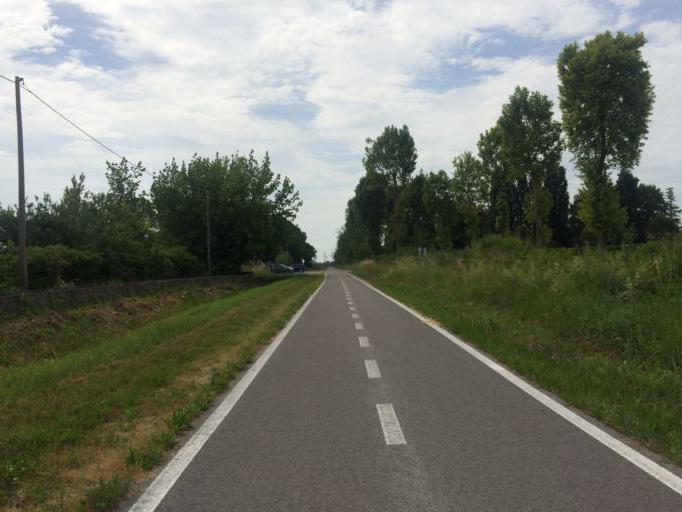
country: IT
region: Friuli Venezia Giulia
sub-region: Provincia di Udine
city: Aquileia
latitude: 45.7463
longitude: 13.3814
